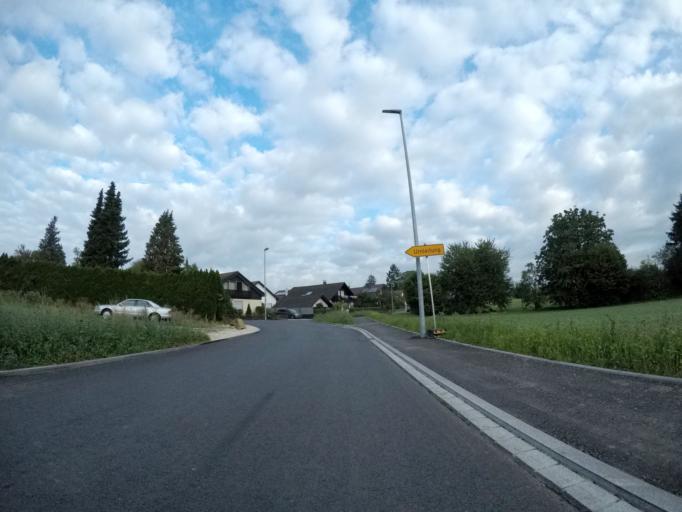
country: DE
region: Baden-Wuerttemberg
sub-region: Tuebingen Region
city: Sickenhausen
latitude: 48.5186
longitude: 9.1820
